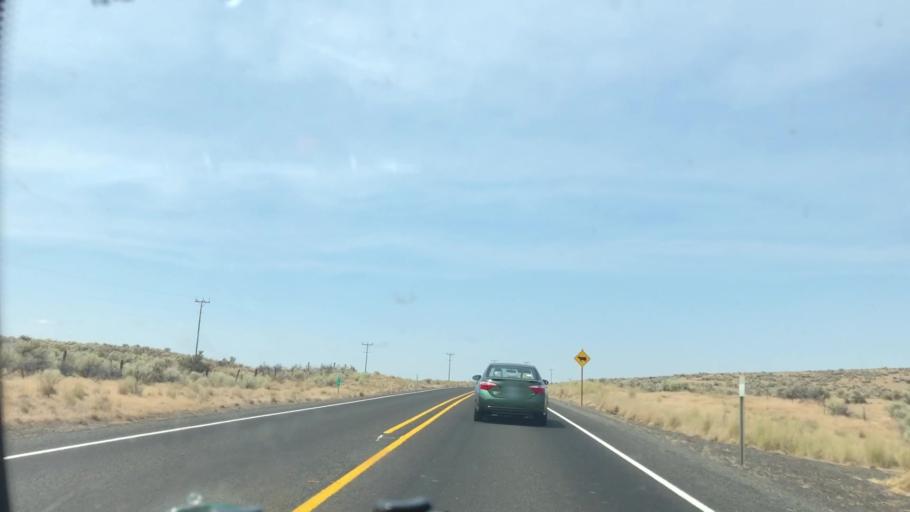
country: US
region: Idaho
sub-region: Owyhee County
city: Murphy
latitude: 42.9931
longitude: -117.0596
